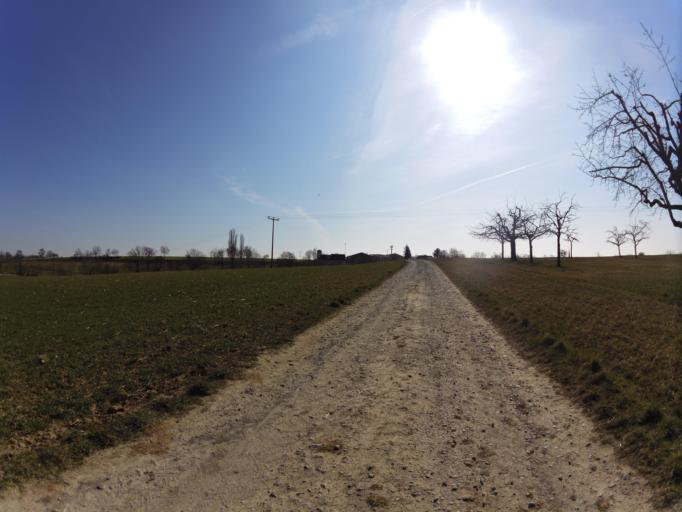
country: DE
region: Bavaria
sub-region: Regierungsbezirk Unterfranken
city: Prosselsheim
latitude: 49.8246
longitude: 10.1122
